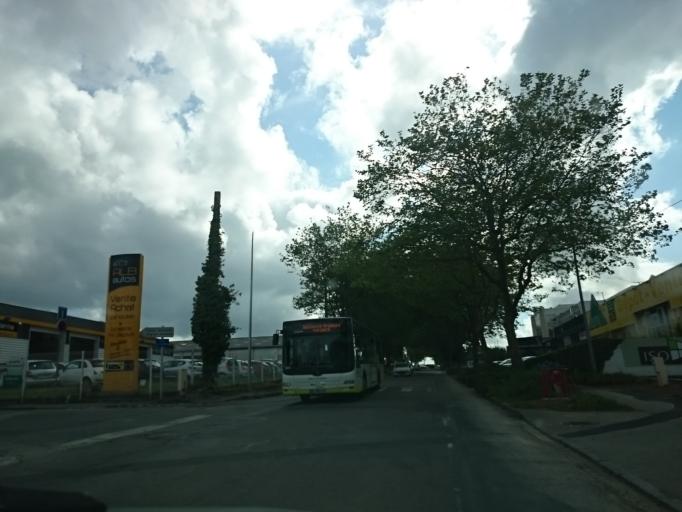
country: FR
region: Brittany
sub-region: Departement du Finistere
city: Brest
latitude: 48.4110
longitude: -4.4594
